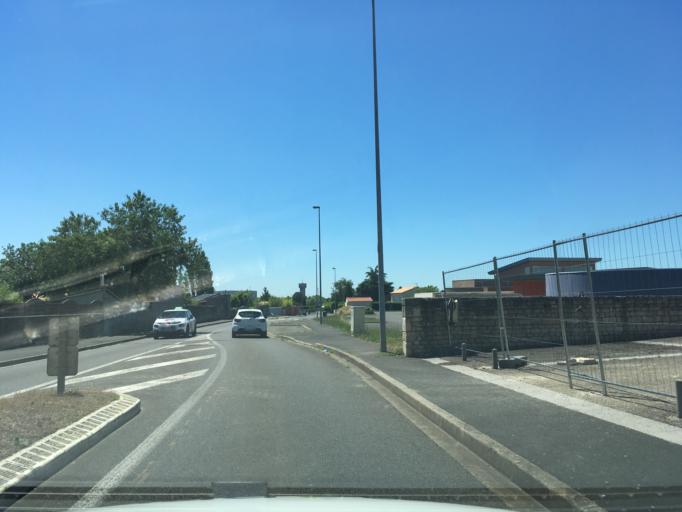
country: FR
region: Poitou-Charentes
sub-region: Departement des Deux-Sevres
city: Niort
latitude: 46.3439
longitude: -0.4403
